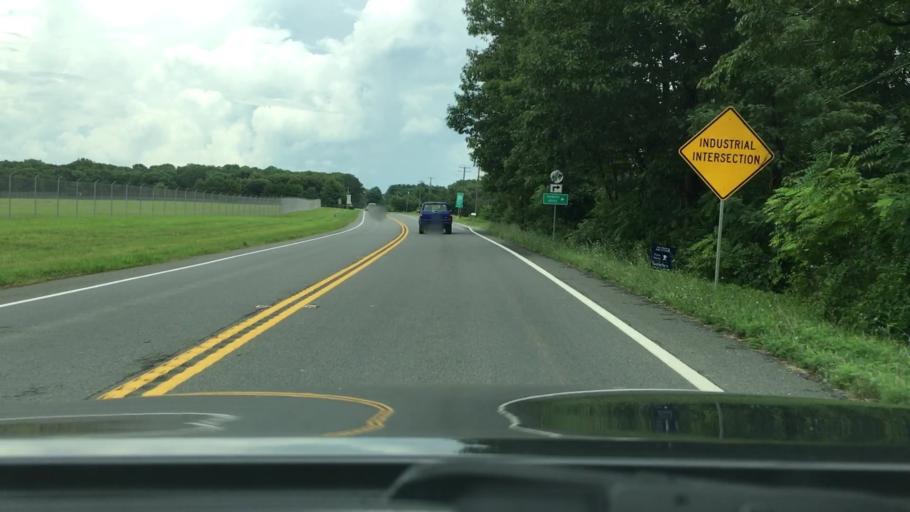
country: US
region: Virginia
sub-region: Orange County
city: Orange
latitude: 38.2479
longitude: -78.0387
